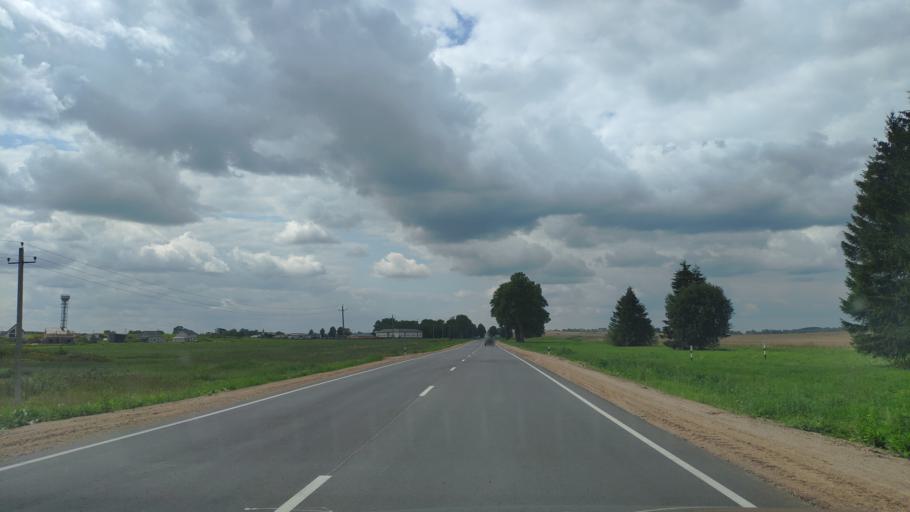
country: BY
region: Minsk
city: Zaslawye
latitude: 54.0055
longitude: 27.3447
